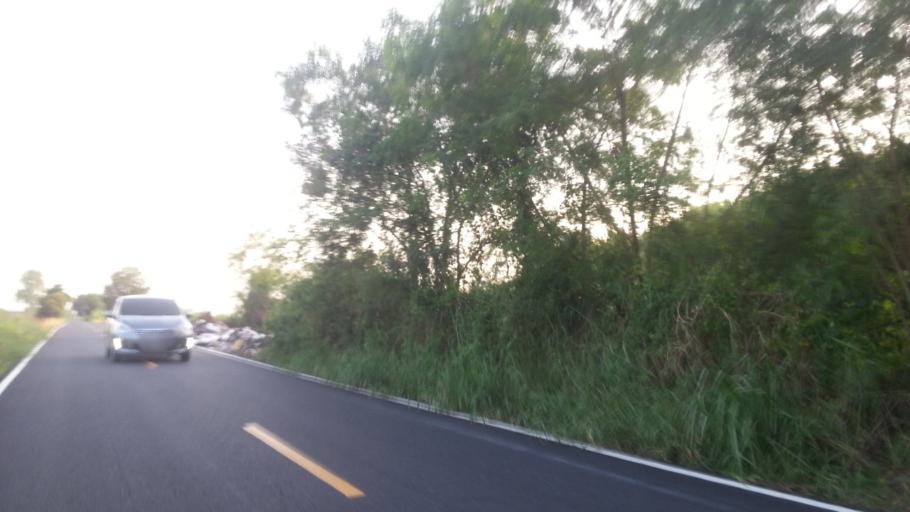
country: TH
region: Pathum Thani
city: Nong Suea
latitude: 14.0454
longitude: 100.8571
